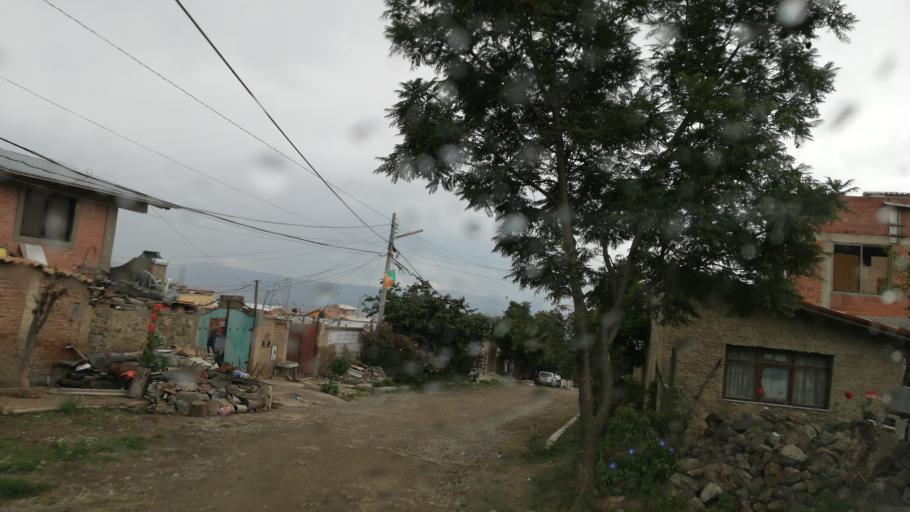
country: BO
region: Cochabamba
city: Cochabamba
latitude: -17.3311
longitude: -66.1942
